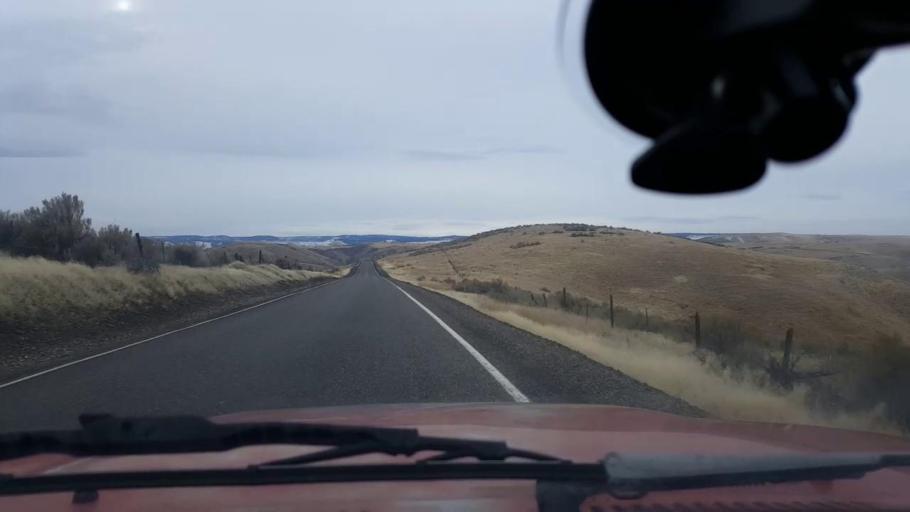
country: US
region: Washington
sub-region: Asotin County
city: Clarkston Heights-Vineland
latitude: 46.3385
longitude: -117.2762
